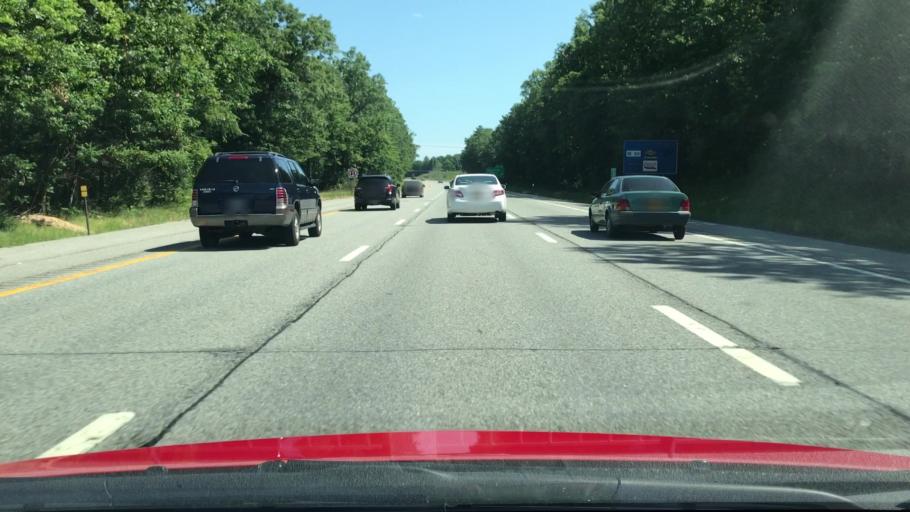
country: US
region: New York
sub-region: Saratoga County
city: Saratoga Springs
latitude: 43.1636
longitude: -73.7166
